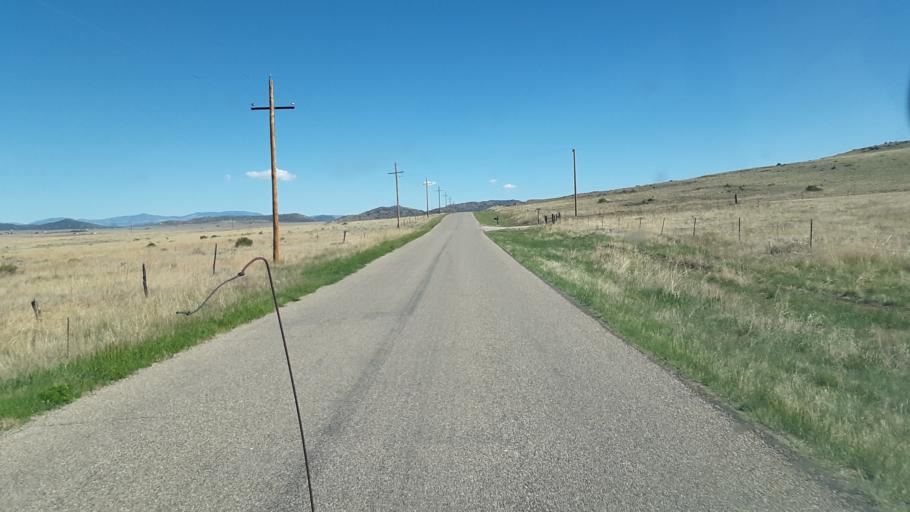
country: US
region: Colorado
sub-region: Custer County
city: Westcliffe
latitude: 38.1766
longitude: -105.4617
